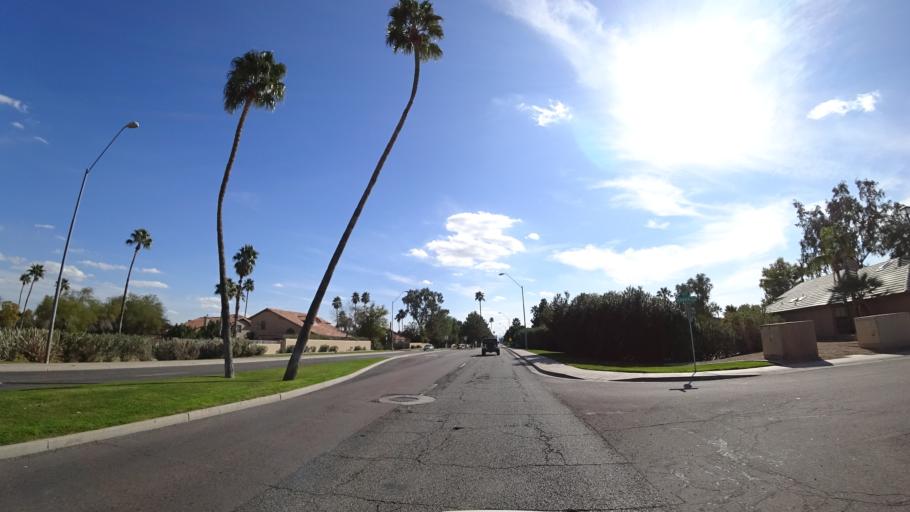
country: US
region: Arizona
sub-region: Maricopa County
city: Sun City
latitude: 33.6628
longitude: -112.2205
